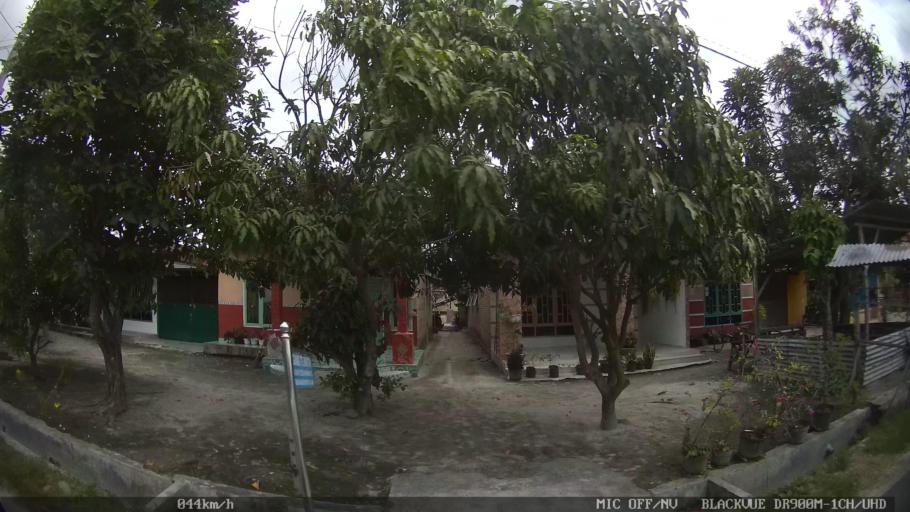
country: ID
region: North Sumatra
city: Percut
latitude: 3.5691
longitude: 98.8632
